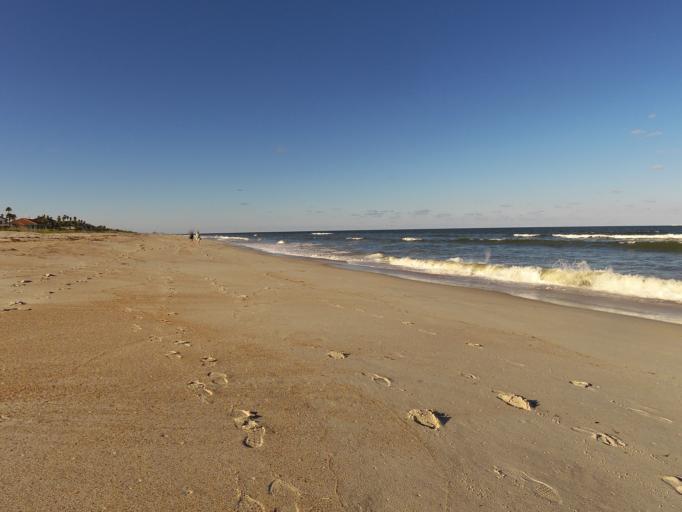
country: US
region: Florida
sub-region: Saint Johns County
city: Sawgrass
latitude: 30.1976
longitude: -81.3650
